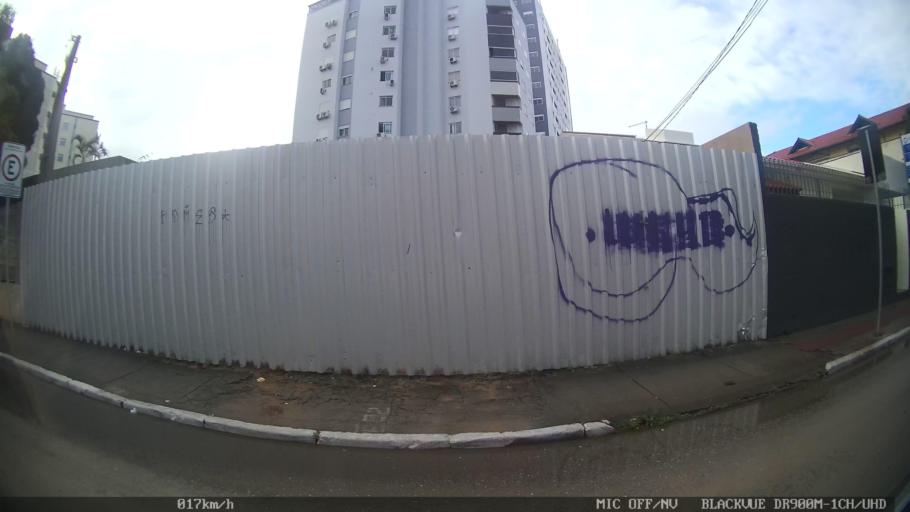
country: BR
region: Santa Catarina
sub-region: Sao Jose
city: Campinas
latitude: -27.5930
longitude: -48.6125
